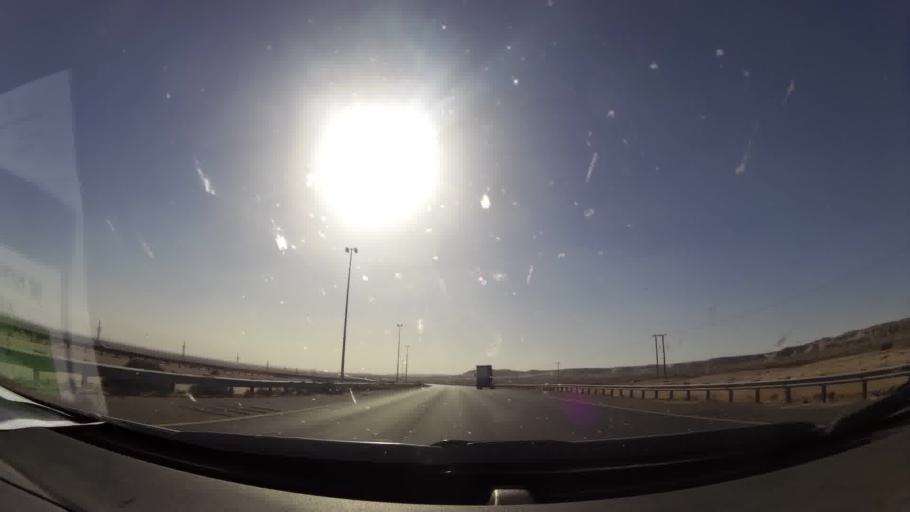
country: KW
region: Al Asimah
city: Kuwait City
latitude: 29.5180
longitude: 47.8083
